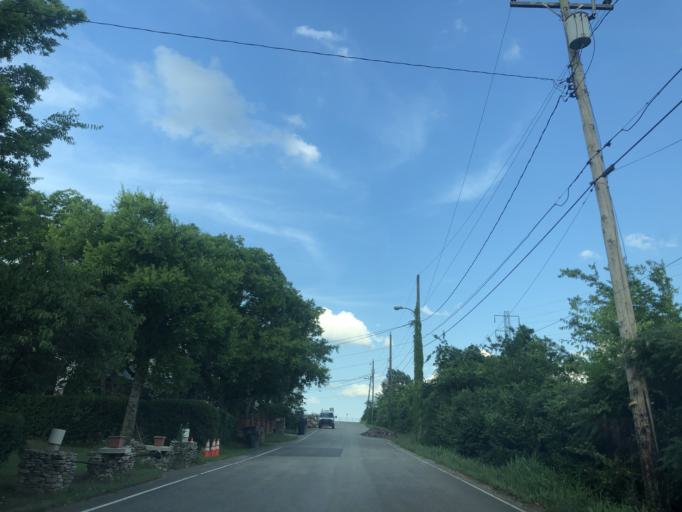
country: US
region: Tennessee
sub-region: Davidson County
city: Nashville
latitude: 36.2121
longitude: -86.7780
